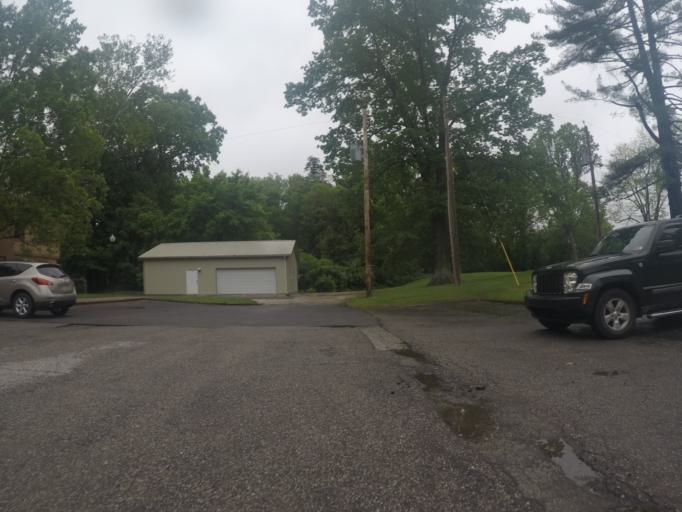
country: US
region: West Virginia
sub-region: Cabell County
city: Barboursville
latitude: 38.4247
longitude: -82.3028
